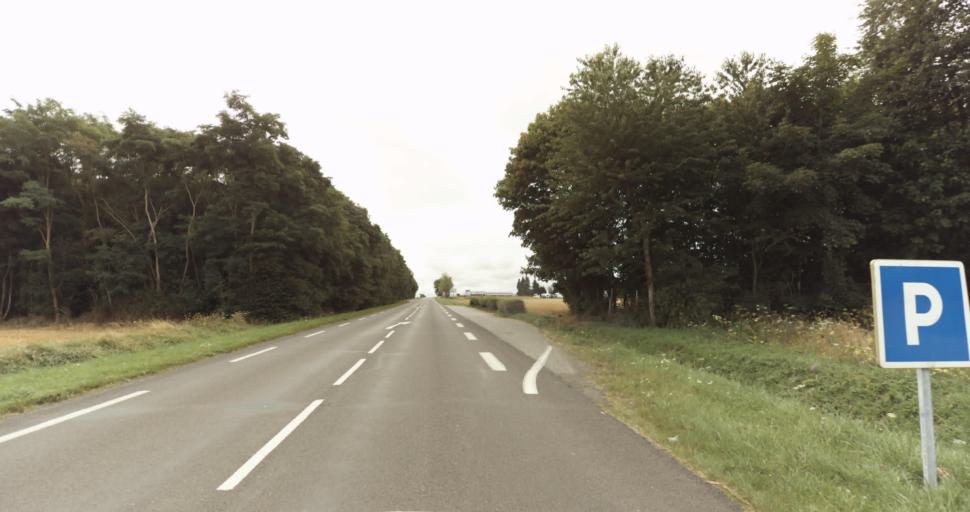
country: FR
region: Haute-Normandie
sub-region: Departement de l'Eure
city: Evreux
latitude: 48.9634
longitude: 1.1606
